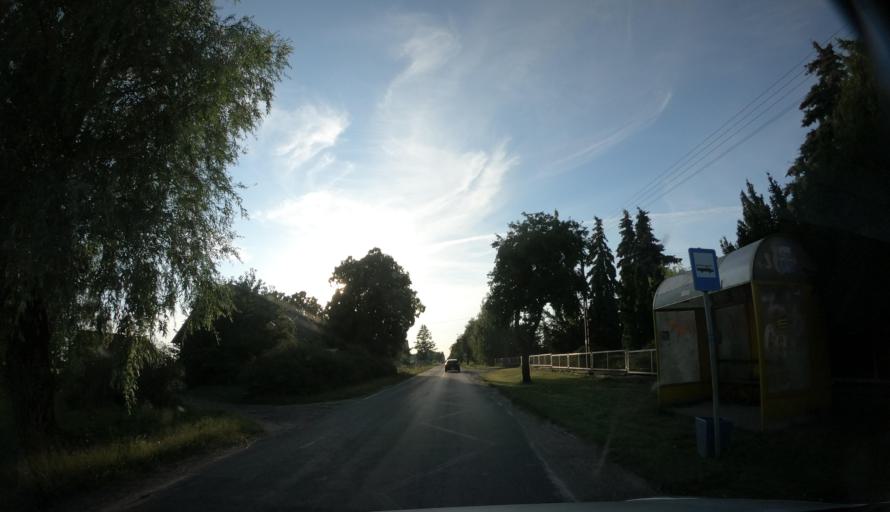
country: PL
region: Kujawsko-Pomorskie
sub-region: Powiat swiecki
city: Pruszcz
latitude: 53.2465
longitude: 18.2040
